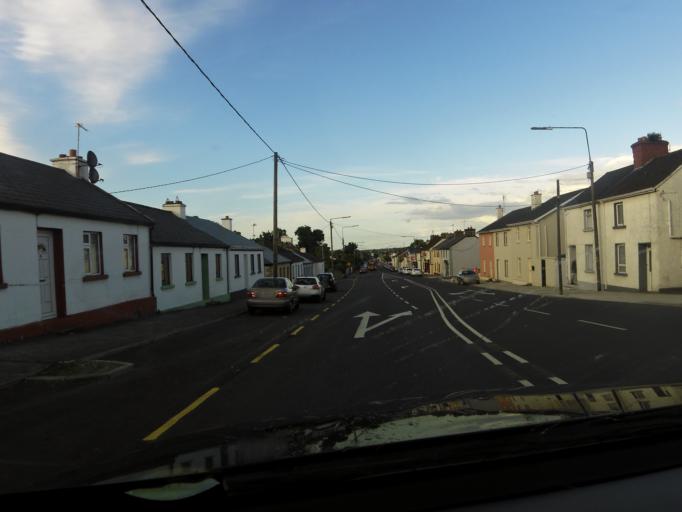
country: IE
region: Connaught
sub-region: County Galway
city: Ballinasloe
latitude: 53.3249
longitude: -8.2373
